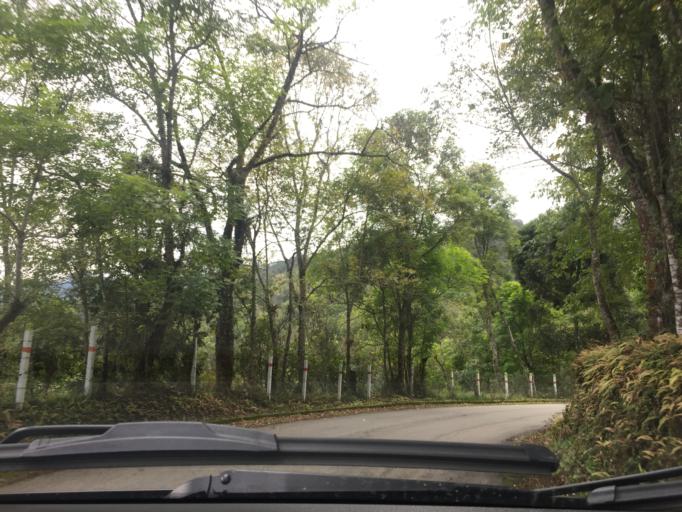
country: CO
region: Cundinamarca
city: Supata
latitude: 5.0526
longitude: -74.2395
